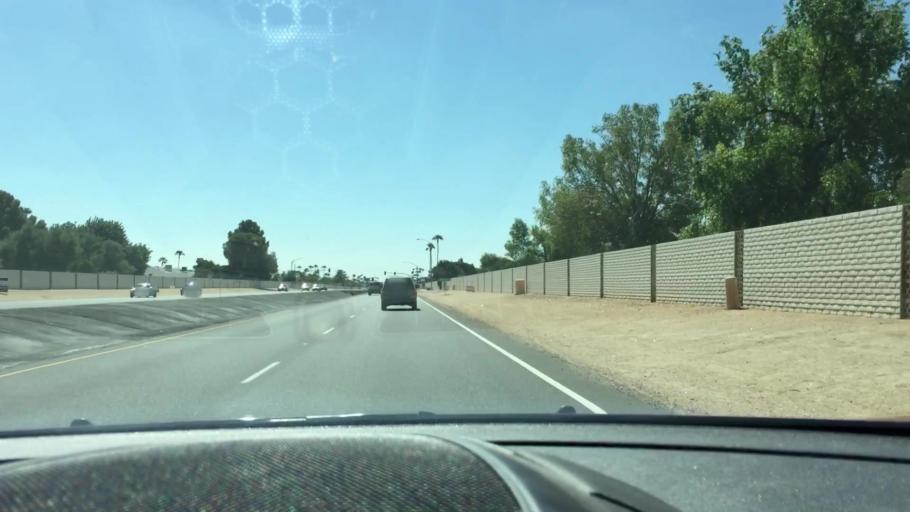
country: US
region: Arizona
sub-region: Maricopa County
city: Sun City
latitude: 33.6492
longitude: -112.2779
